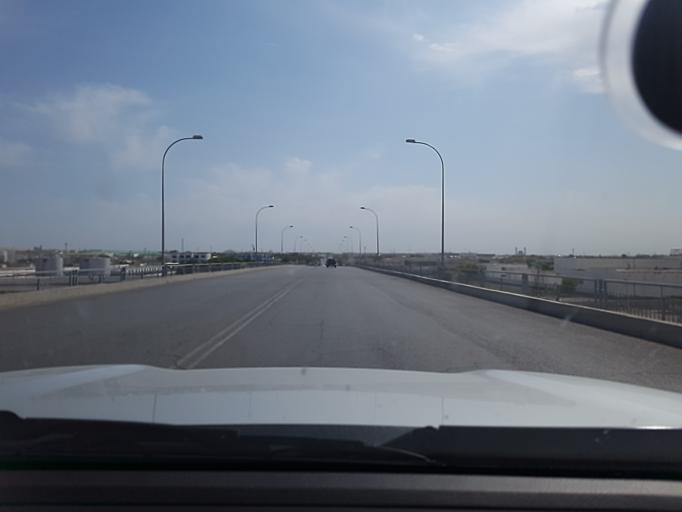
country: TM
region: Dasoguz
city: Dasoguz
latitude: 41.8635
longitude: 59.9471
